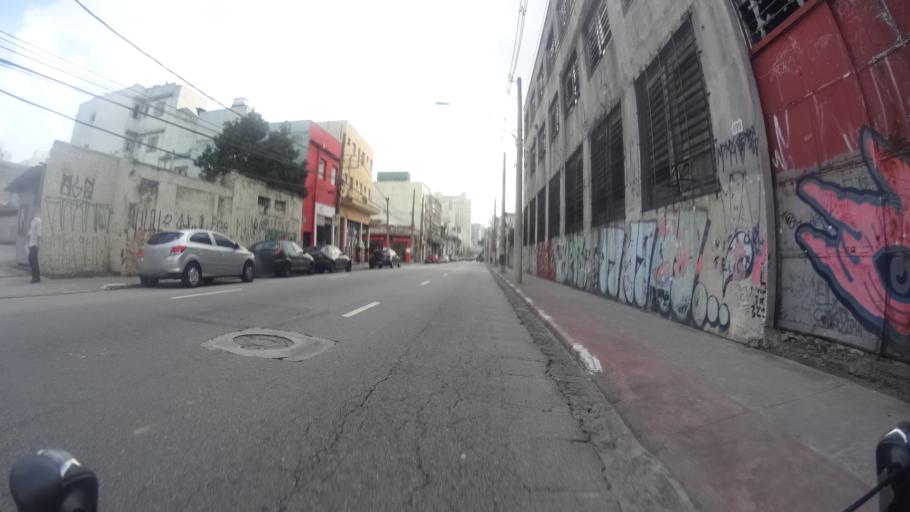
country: BR
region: Sao Paulo
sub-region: Sao Paulo
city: Sao Paulo
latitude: -23.5538
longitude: -46.6183
